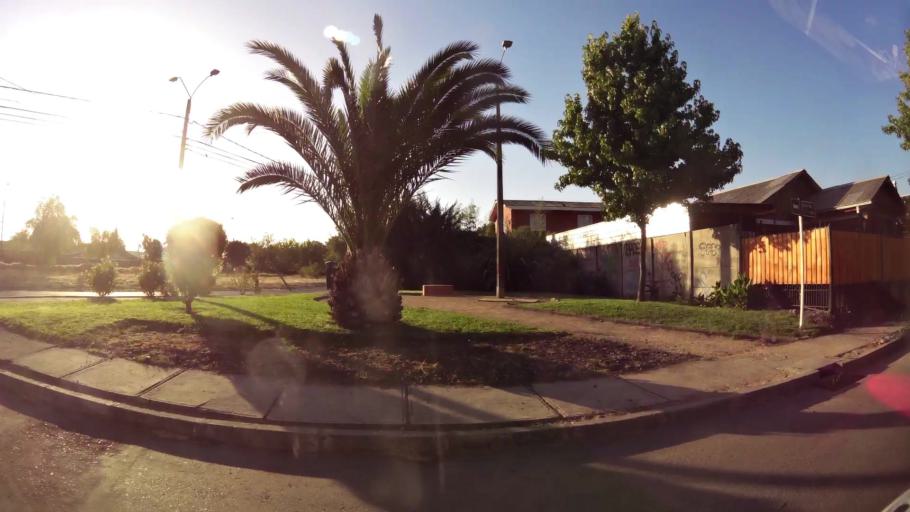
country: CL
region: Maule
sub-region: Provincia de Talca
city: Talca
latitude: -35.4453
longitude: -71.6746
